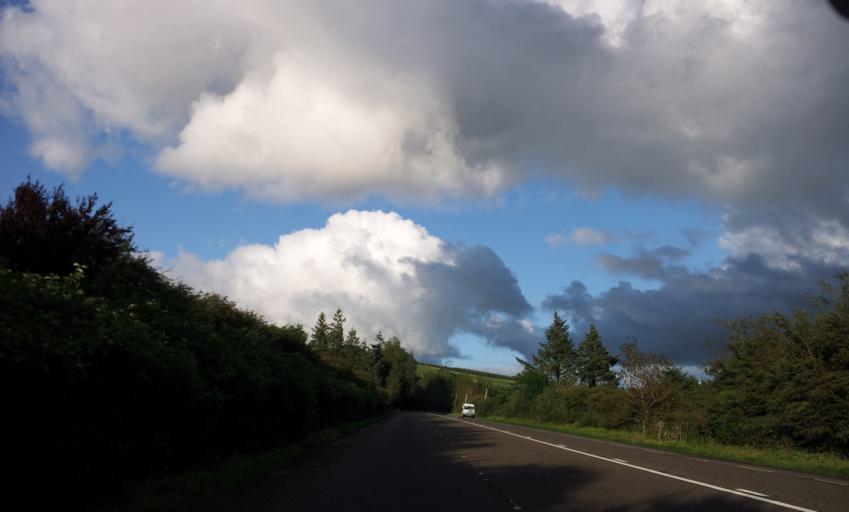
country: IE
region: Munster
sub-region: Ciarrai
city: Castleisland
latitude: 52.2647
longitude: -9.4485
